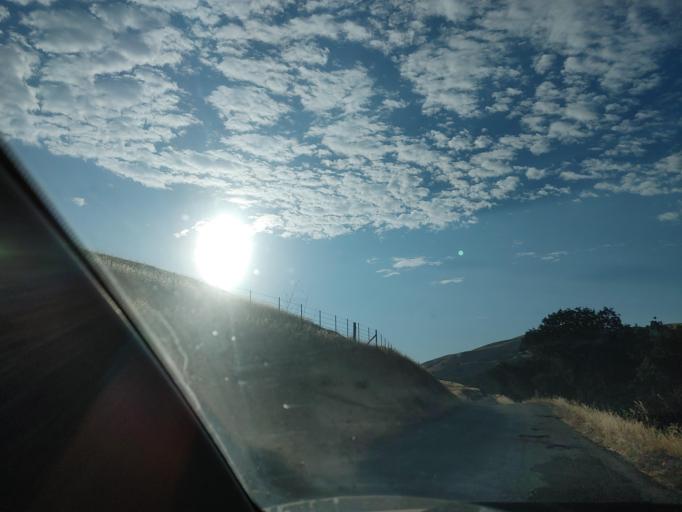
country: US
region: California
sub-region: San Benito County
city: Ridgemark
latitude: 36.7718
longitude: -121.2221
